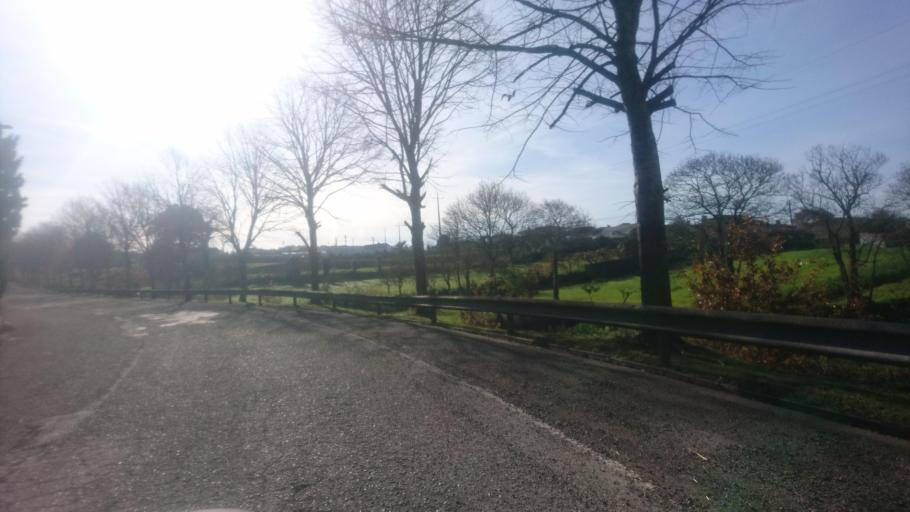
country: PT
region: Aveiro
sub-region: Santa Maria da Feira
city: Rio Meao
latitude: 40.9297
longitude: -8.5770
